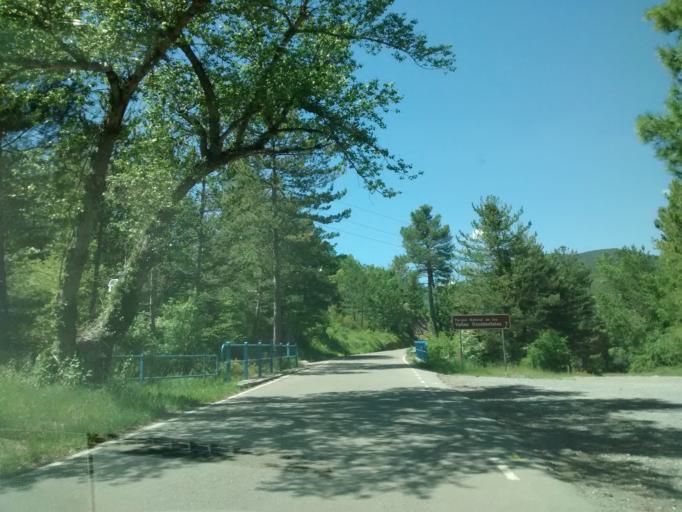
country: ES
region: Aragon
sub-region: Provincia de Huesca
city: Castiello de Jaca
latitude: 42.6514
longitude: -0.5605
